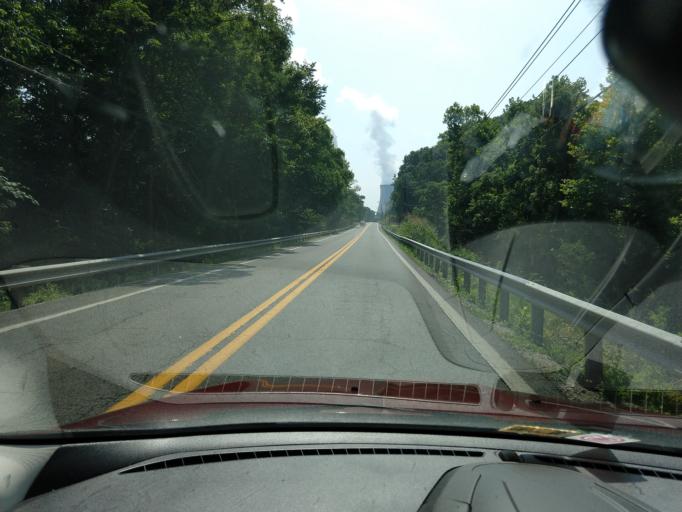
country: US
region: West Virginia
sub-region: Mason County
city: New Haven
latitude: 38.9846
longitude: -81.9577
